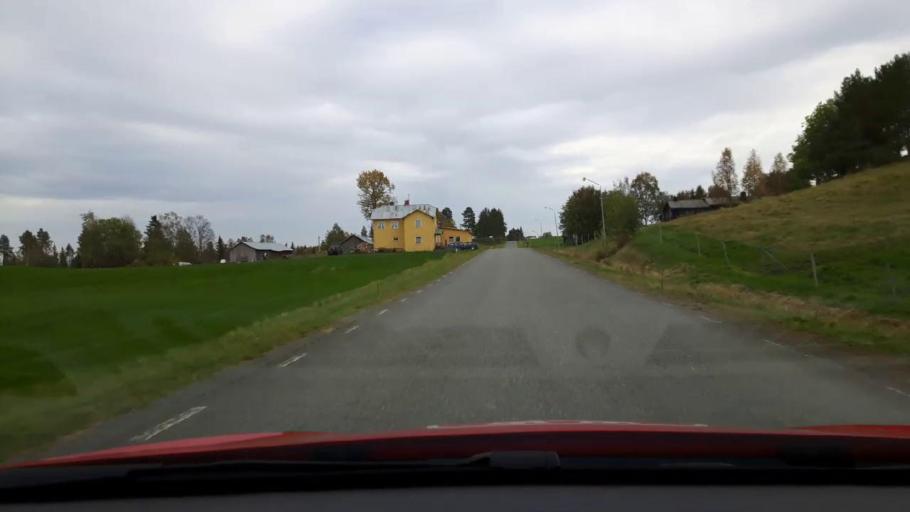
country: SE
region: Jaemtland
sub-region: Krokoms Kommun
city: Krokom
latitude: 63.2313
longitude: 14.1257
